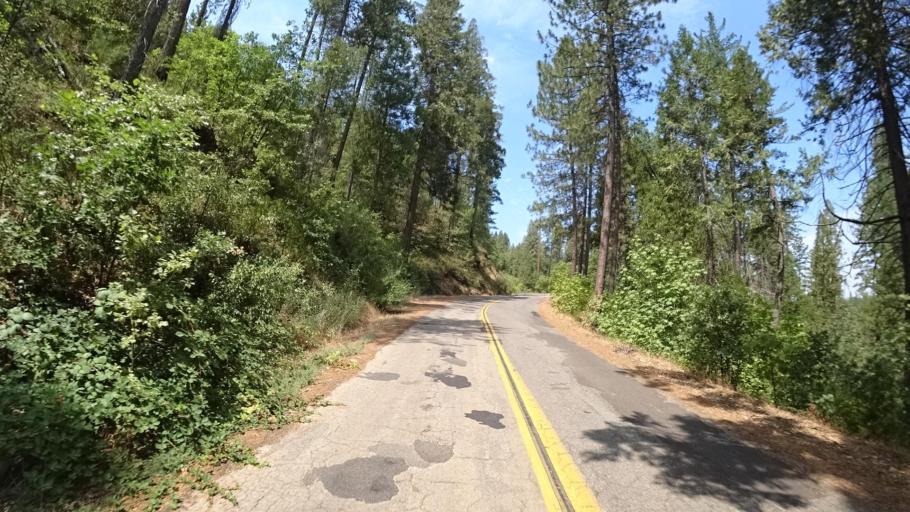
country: US
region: California
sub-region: Mariposa County
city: Midpines
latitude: 37.7543
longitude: -120.0655
